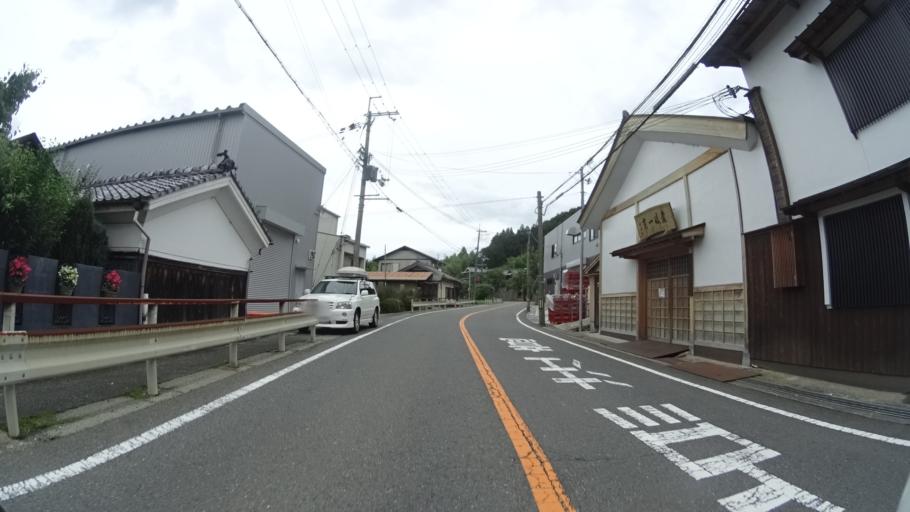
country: JP
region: Kyoto
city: Kameoka
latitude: 34.9768
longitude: 135.4668
